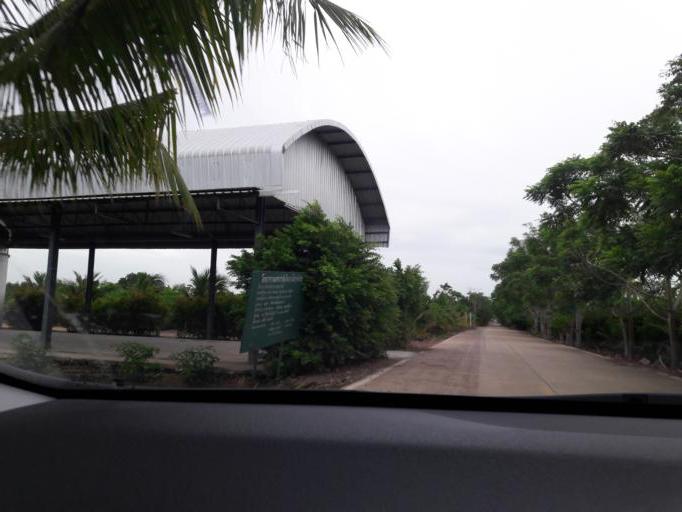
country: TH
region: Ratchaburi
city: Damnoen Saduak
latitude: 13.5570
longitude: 100.0114
